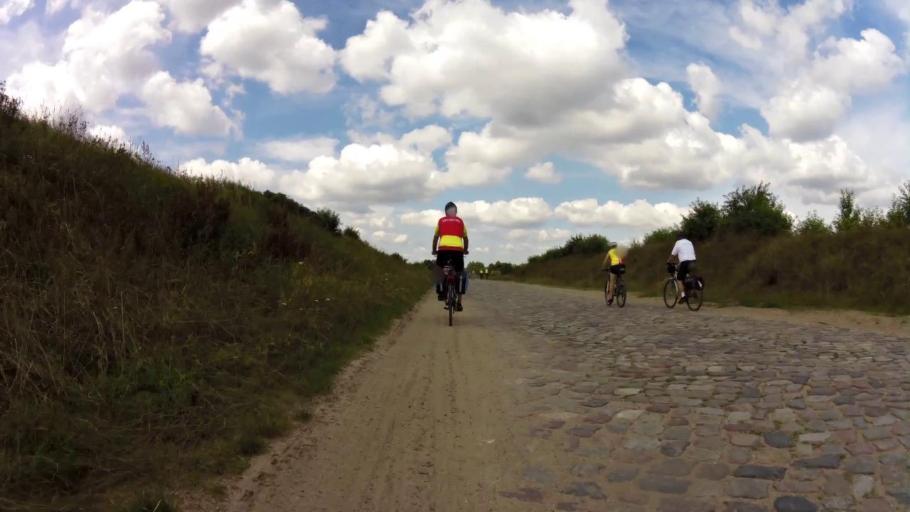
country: PL
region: West Pomeranian Voivodeship
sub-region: Powiat drawski
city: Drawsko Pomorskie
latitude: 53.4513
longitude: 15.7673
